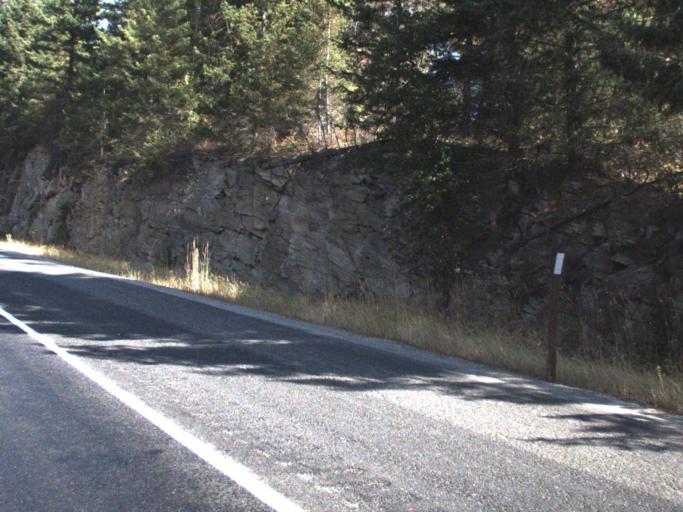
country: US
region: Washington
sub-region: Spokane County
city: Deer Park
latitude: 48.0964
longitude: -117.3088
